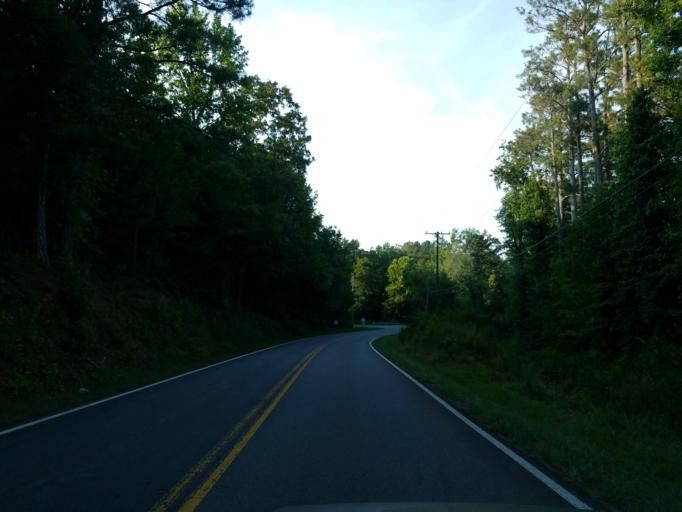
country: US
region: Georgia
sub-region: Pickens County
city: Jasper
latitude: 34.5485
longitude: -84.5424
